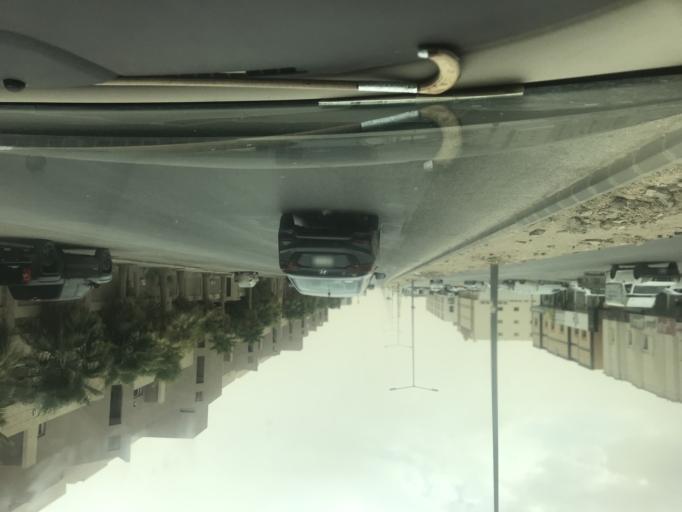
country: SA
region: Ar Riyad
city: Riyadh
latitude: 24.8094
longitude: 46.6131
